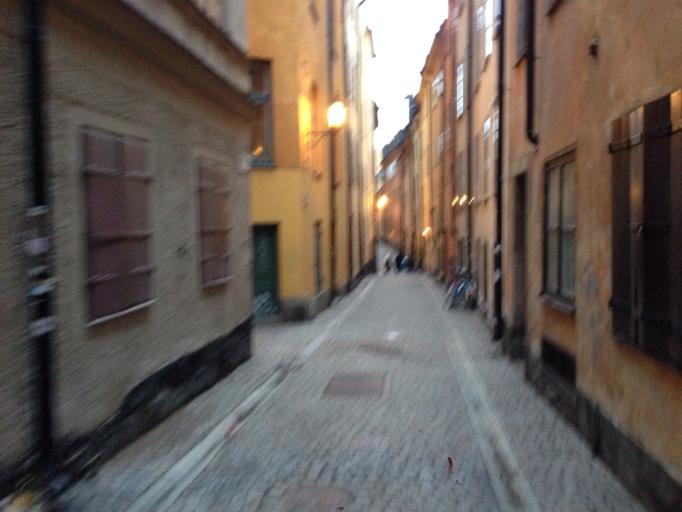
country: SE
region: Stockholm
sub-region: Stockholms Kommun
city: Stockholm
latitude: 59.3244
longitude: 18.0704
